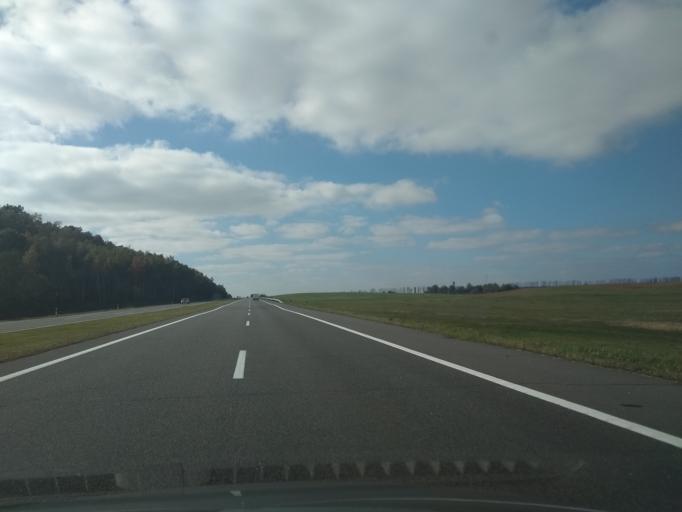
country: BY
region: Minsk
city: Snow
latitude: 53.2440
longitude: 26.2009
